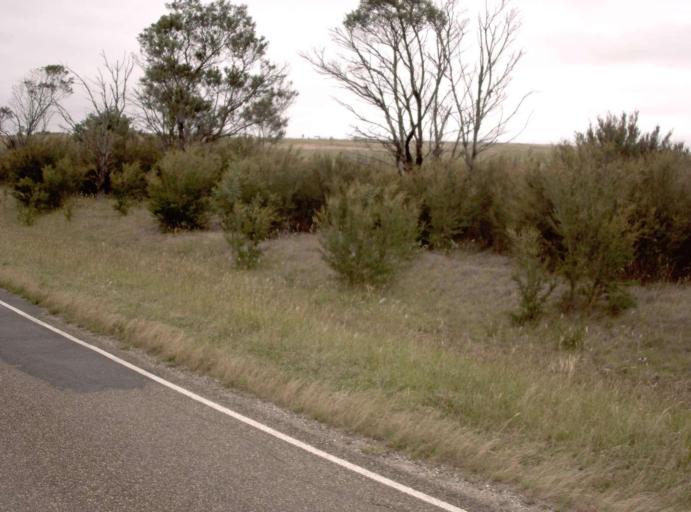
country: AU
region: Victoria
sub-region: Wellington
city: Heyfield
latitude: -38.1316
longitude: 146.7885
